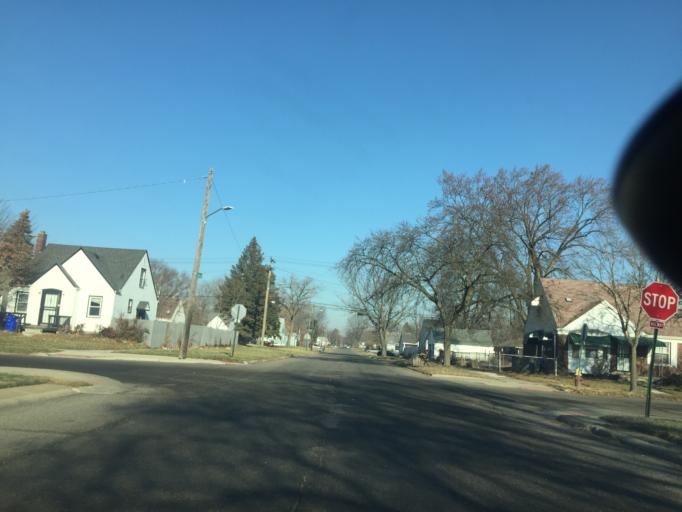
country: US
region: Michigan
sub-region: Wayne County
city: Harper Woods
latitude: 42.4363
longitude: -82.9558
